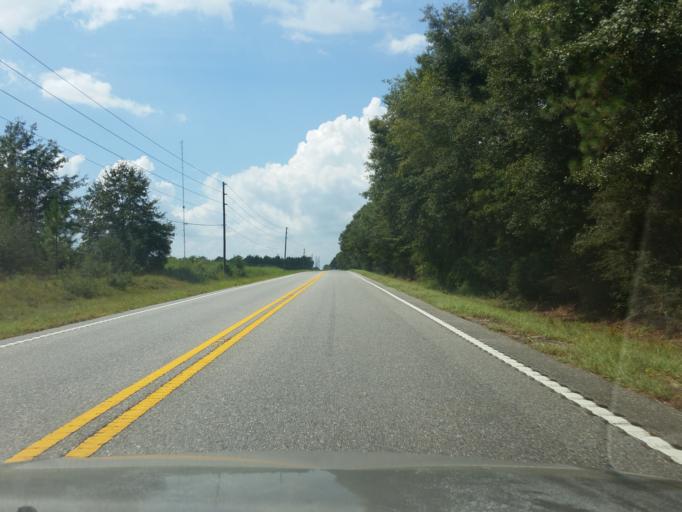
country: US
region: Alabama
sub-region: Baldwin County
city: Elberta
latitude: 30.5328
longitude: -87.5230
